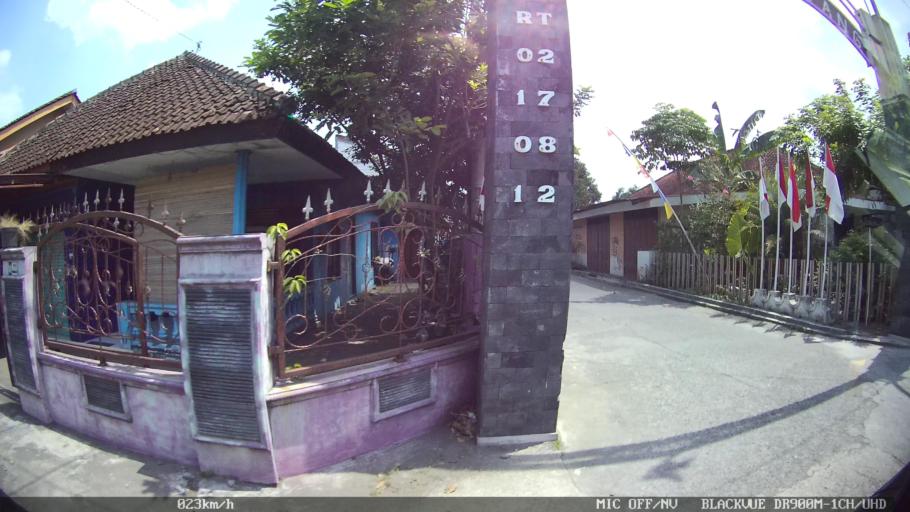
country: ID
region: Daerah Istimewa Yogyakarta
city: Yogyakarta
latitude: -7.8207
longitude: 110.4073
